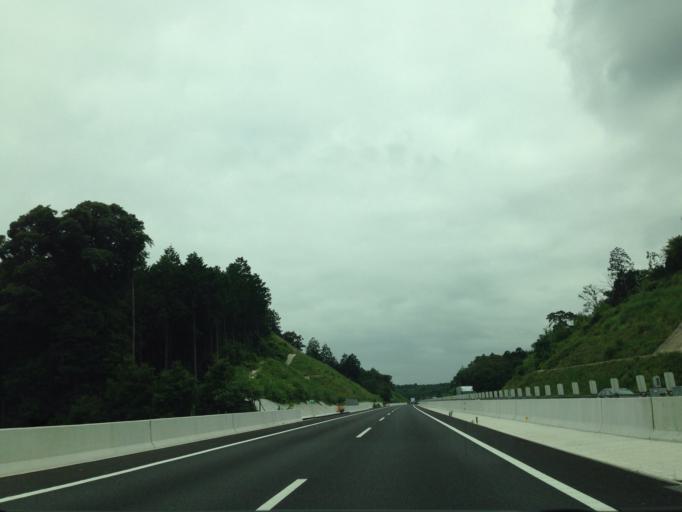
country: JP
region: Aichi
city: Okazaki
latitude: 34.9783
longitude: 137.2428
